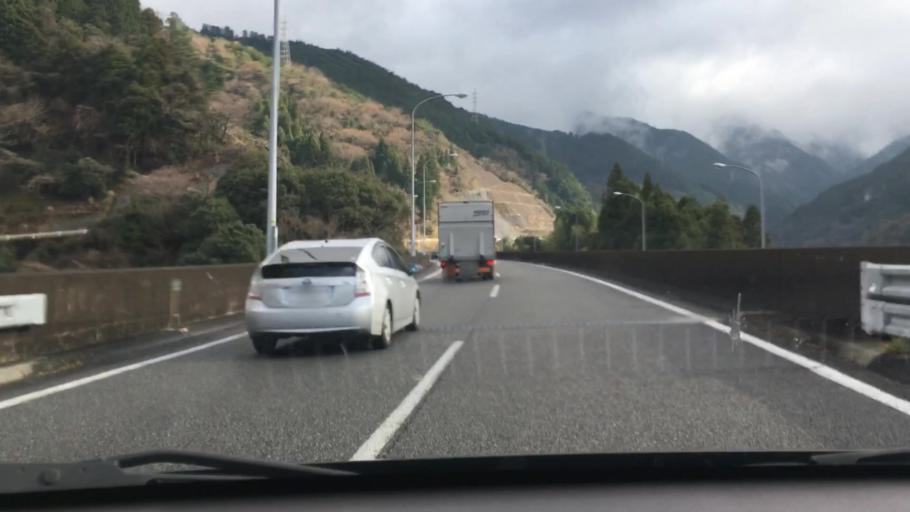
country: JP
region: Kumamoto
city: Yatsushiro
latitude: 32.4014
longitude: 130.6990
